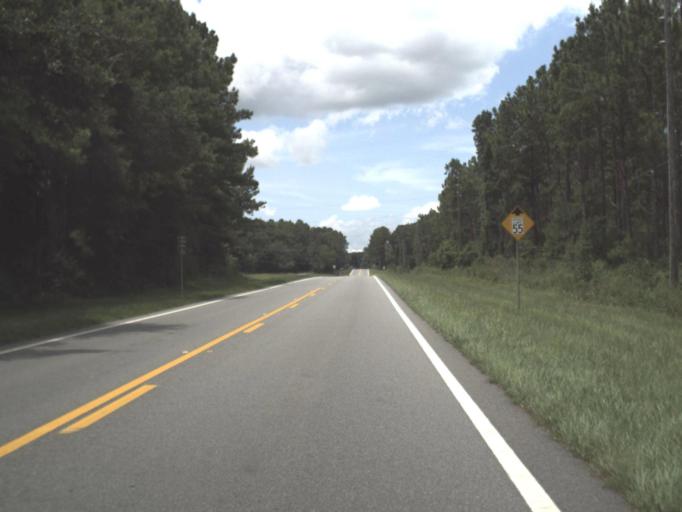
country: US
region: Florida
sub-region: Madison County
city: Madison
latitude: 30.5843
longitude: -83.3545
